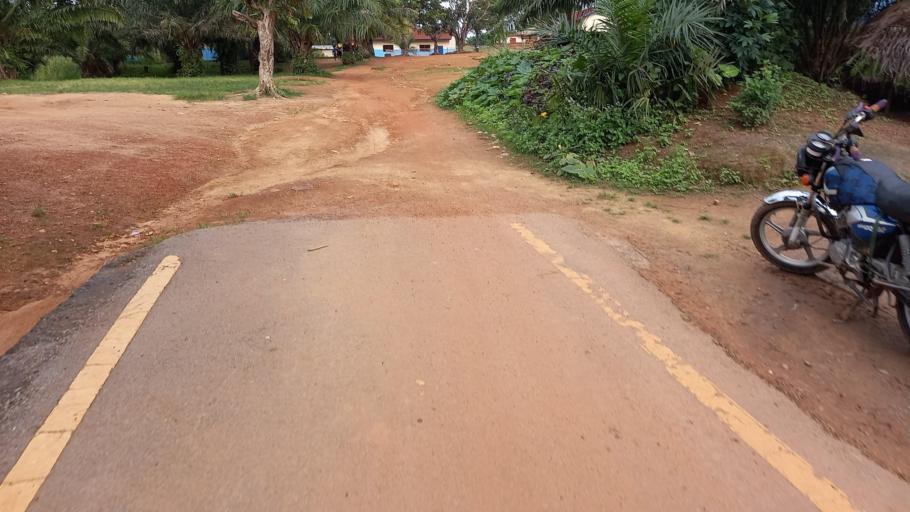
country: SL
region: Eastern Province
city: Kailahun
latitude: 8.2846
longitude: -10.5736
